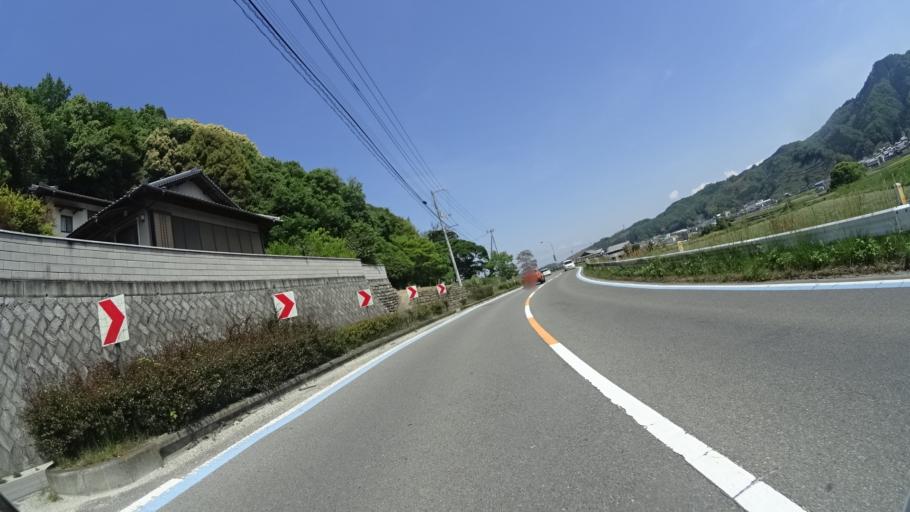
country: JP
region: Ehime
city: Hojo
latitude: 34.0266
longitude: 132.9483
